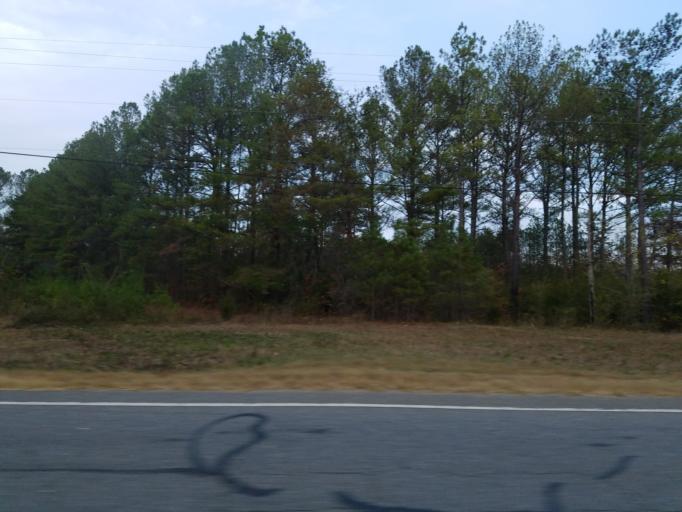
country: US
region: Georgia
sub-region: Murray County
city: Chatsworth
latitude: 34.5952
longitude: -84.7499
